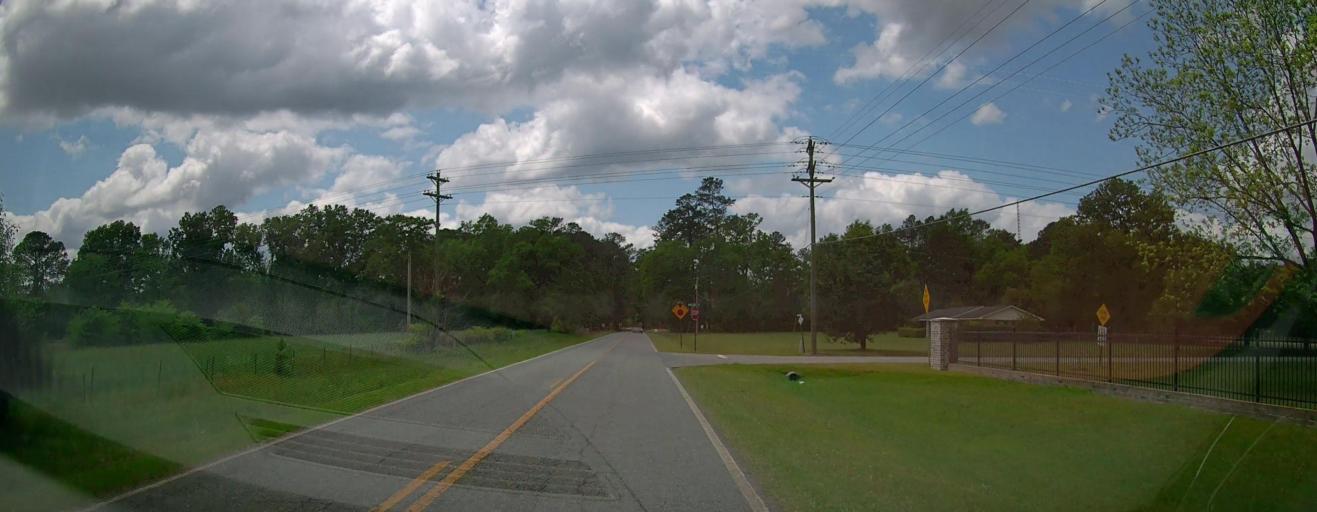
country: US
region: Georgia
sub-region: Laurens County
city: Dublin
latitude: 32.5879
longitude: -82.9406
